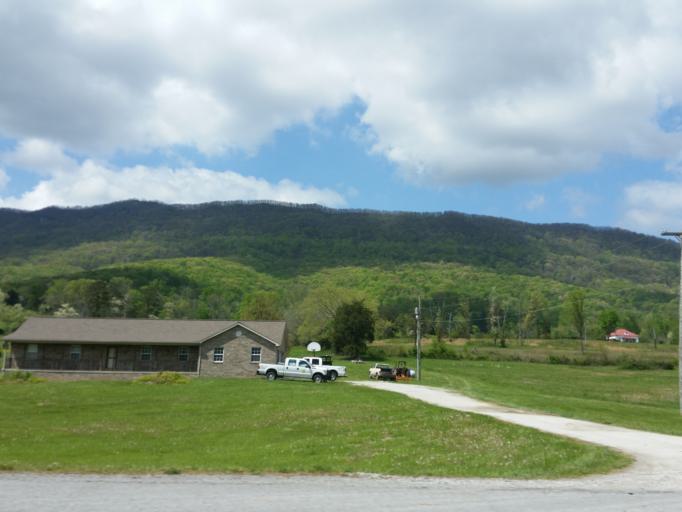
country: US
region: Tennessee
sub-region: Campbell County
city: Fincastle
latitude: 36.4533
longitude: -83.9143
